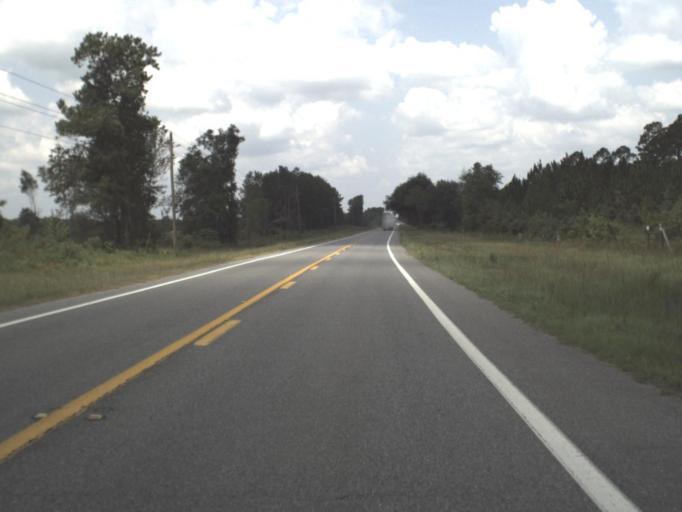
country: US
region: Florida
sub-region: Madison County
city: Madison
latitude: 30.4866
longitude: -83.1854
